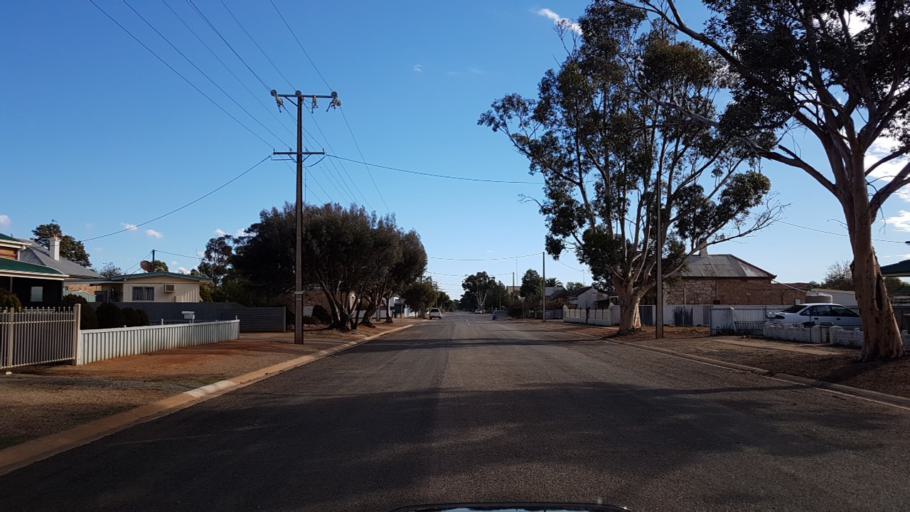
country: AU
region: South Australia
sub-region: Peterborough
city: Peterborough
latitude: -32.9717
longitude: 138.8433
